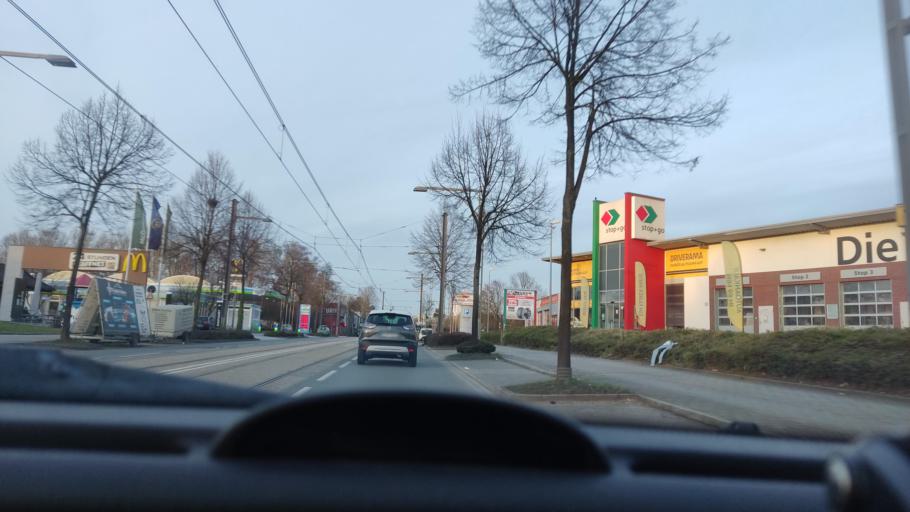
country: DE
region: North Rhine-Westphalia
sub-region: Regierungsbezirk Arnsberg
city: Dortmund
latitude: 51.5454
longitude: 7.4603
